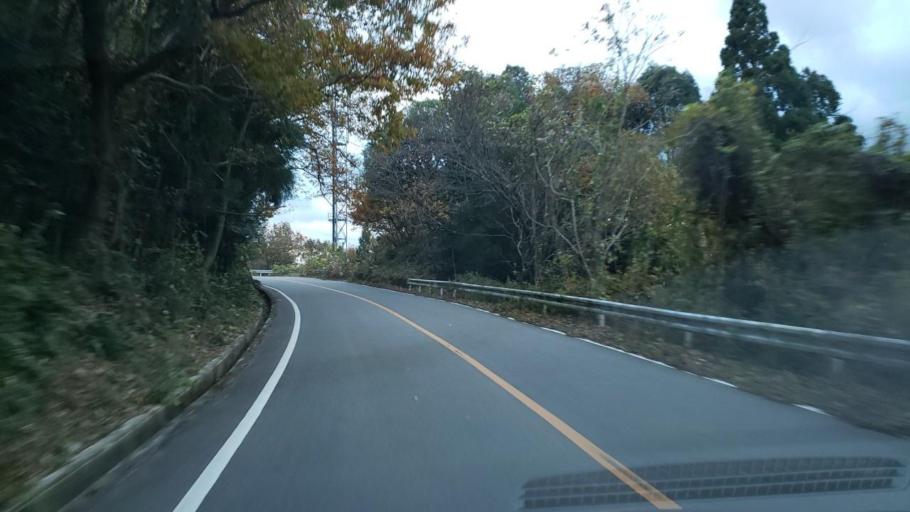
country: JP
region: Tokushima
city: Wakimachi
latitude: 34.0856
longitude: 134.1784
